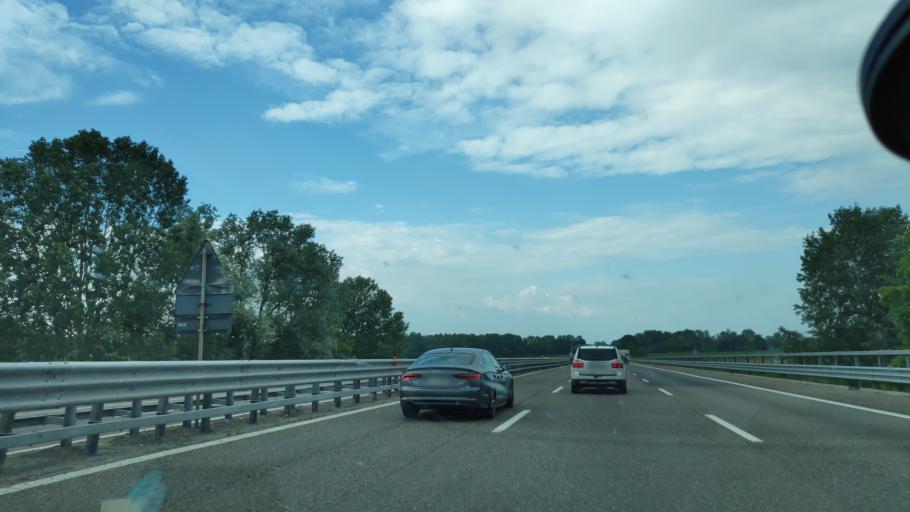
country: IT
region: Lombardy
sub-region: Provincia di Pavia
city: Gropello Cairoli
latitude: 45.1809
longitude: 9.0081
